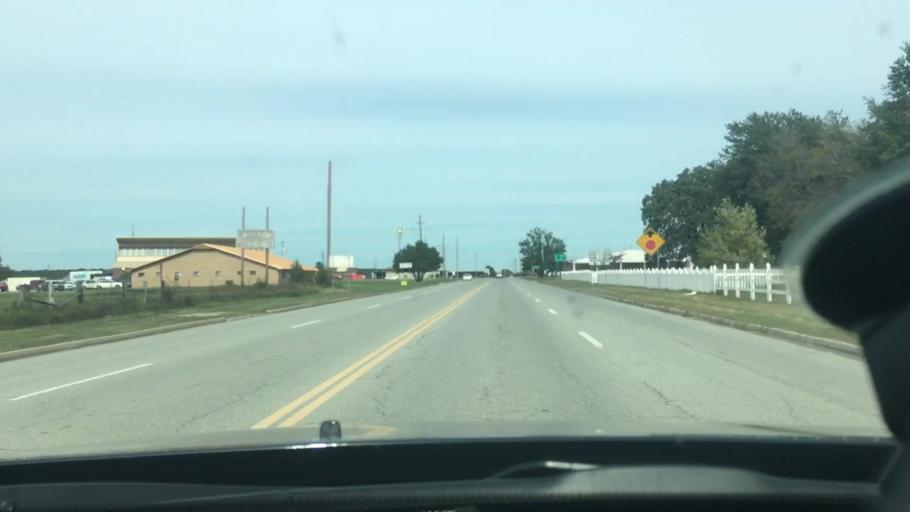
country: US
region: Oklahoma
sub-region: Atoka County
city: Atoka
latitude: 34.3914
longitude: -96.1455
